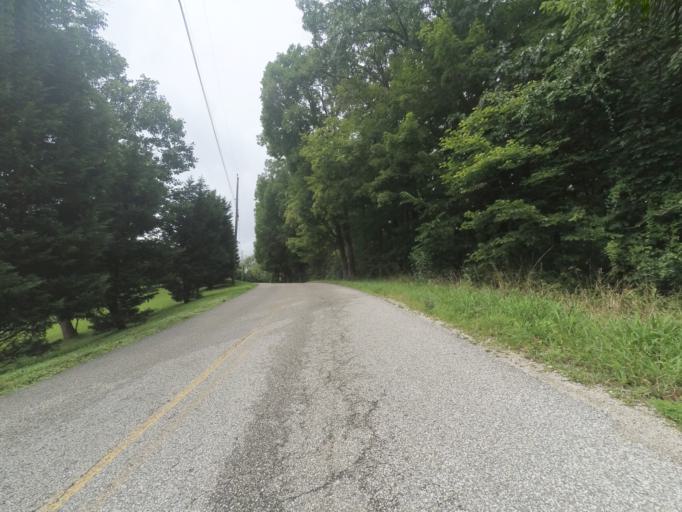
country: US
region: West Virginia
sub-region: Cabell County
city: Huntington
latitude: 38.4330
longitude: -82.4714
